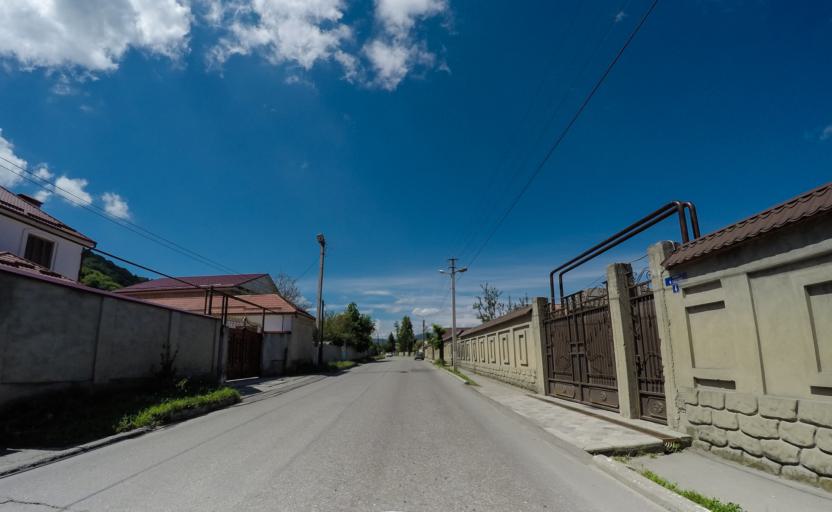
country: RU
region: Kabardino-Balkariya
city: Vol'nyy Aul
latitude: 43.4485
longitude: 43.5888
